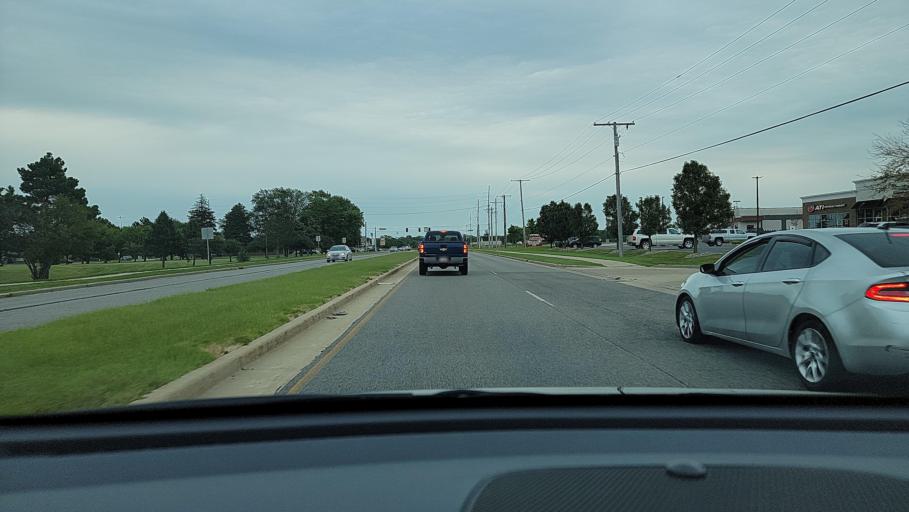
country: US
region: Indiana
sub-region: Porter County
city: Portage
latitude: 41.5505
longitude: -87.1659
